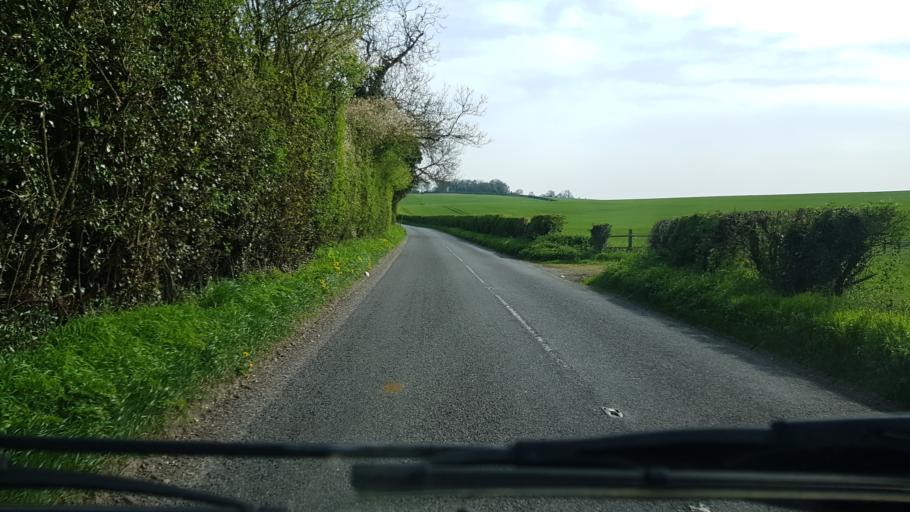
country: GB
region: England
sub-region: Hampshire
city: Overton
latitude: 51.2846
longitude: -1.2624
